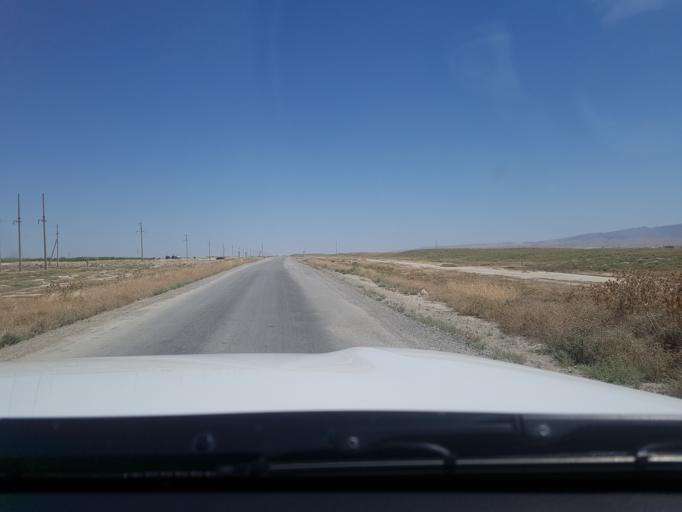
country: IR
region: Razavi Khorasan
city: Kalat-e Naderi
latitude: 37.0707
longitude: 60.1444
